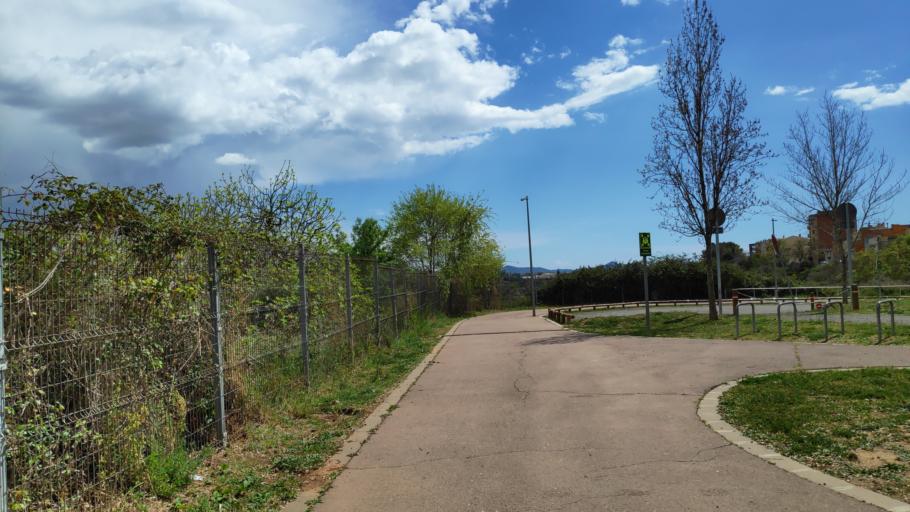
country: ES
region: Catalonia
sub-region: Provincia de Barcelona
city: Sabadell
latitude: 41.5469
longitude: 2.1200
